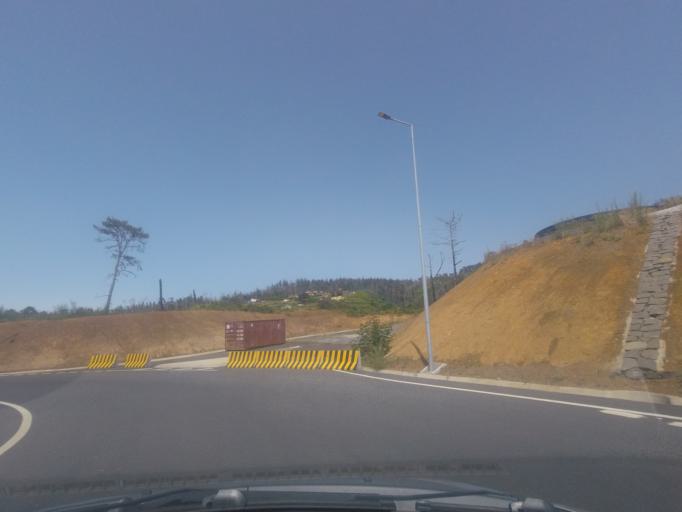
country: PT
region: Madeira
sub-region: Calheta
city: Faja da Ovelha
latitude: 32.8022
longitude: -17.2364
